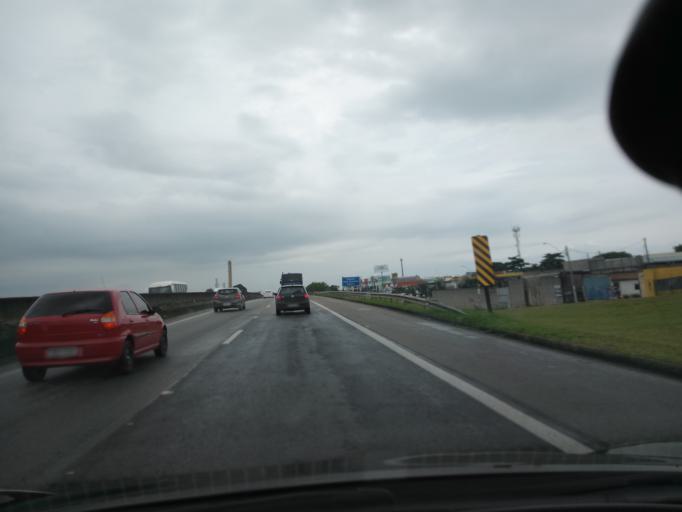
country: BR
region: Sao Paulo
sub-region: Campinas
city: Campinas
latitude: -22.9437
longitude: -47.0884
